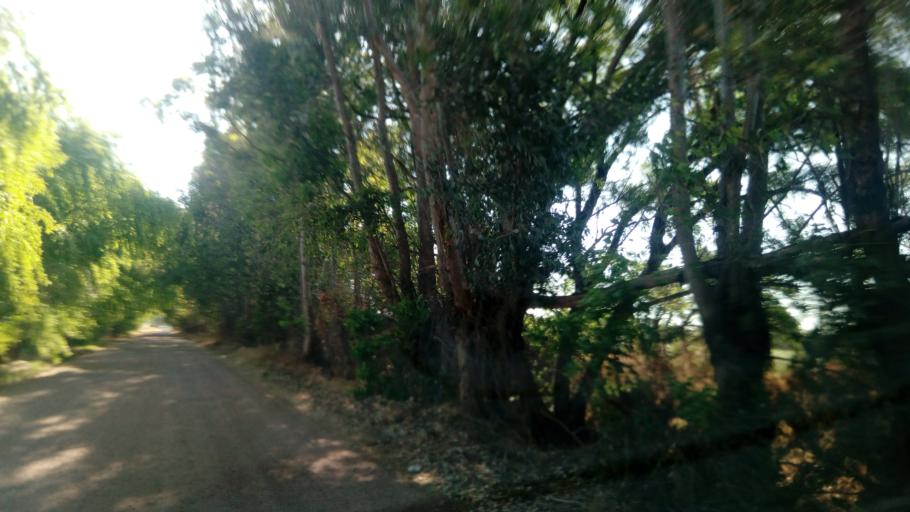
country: MX
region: Durango
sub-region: Durango
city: Jose Refugio Salcido
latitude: 24.0196
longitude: -104.5486
